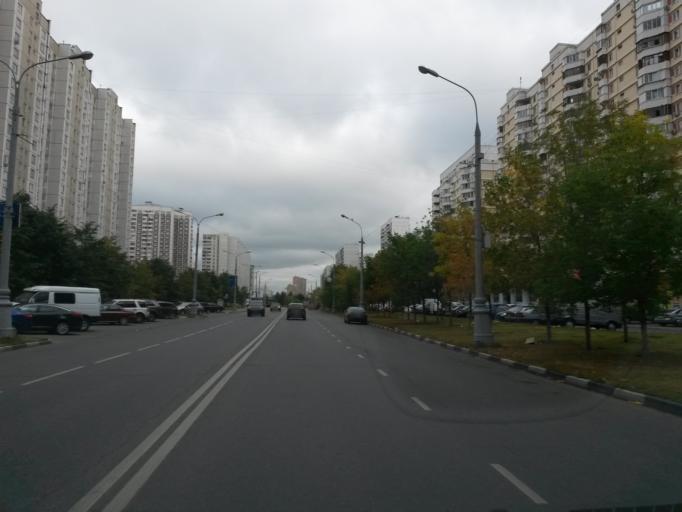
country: RU
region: Moscow
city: Brateyevo
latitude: 55.6538
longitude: 37.7653
